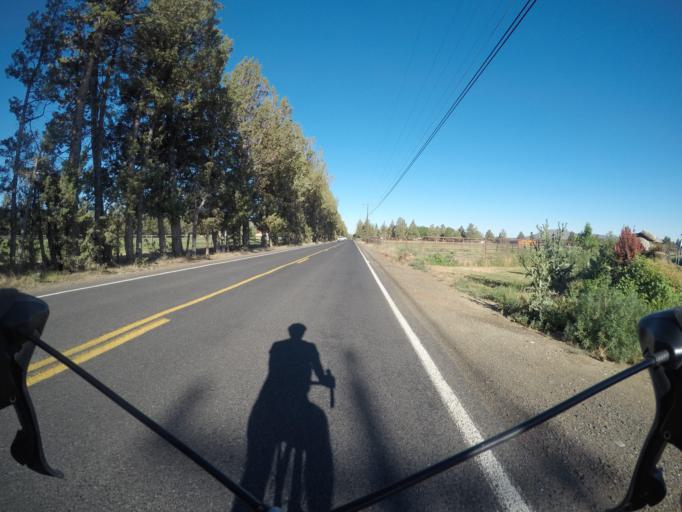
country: US
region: Oregon
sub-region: Deschutes County
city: Redmond
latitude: 44.2186
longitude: -121.2409
